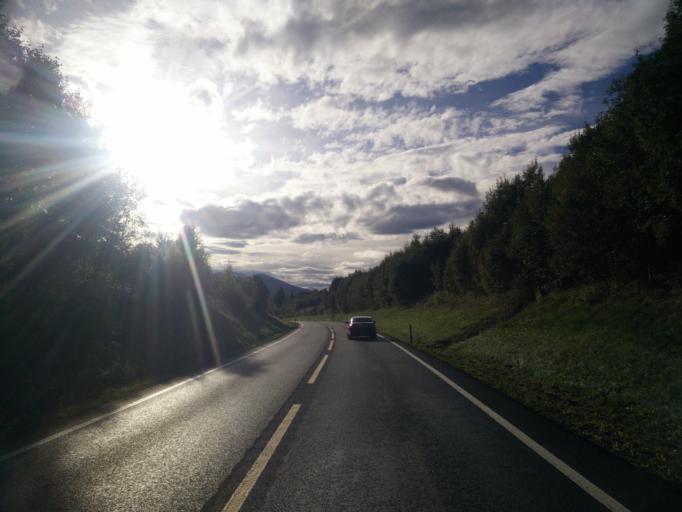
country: NO
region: More og Romsdal
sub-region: Vestnes
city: Vestnes
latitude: 62.6152
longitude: 7.0881
